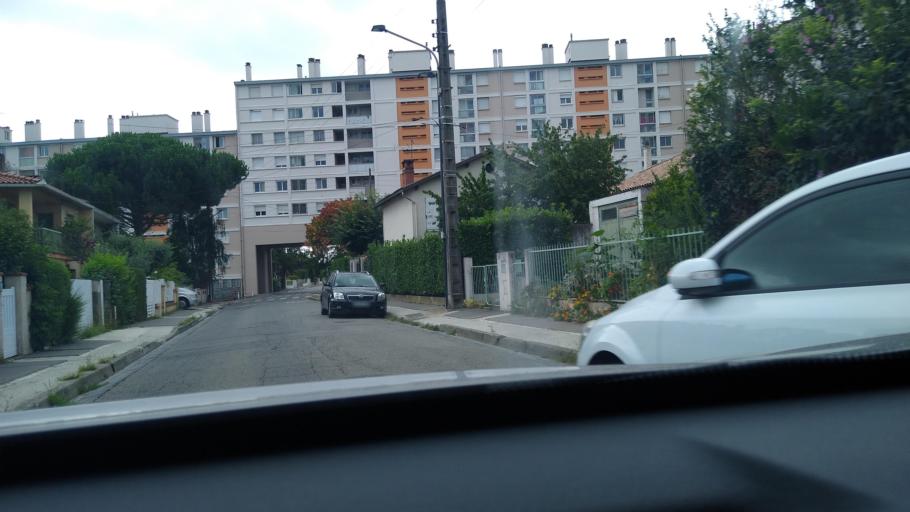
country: FR
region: Midi-Pyrenees
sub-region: Departement de la Haute-Garonne
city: Toulouse
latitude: 43.6135
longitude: 1.4700
